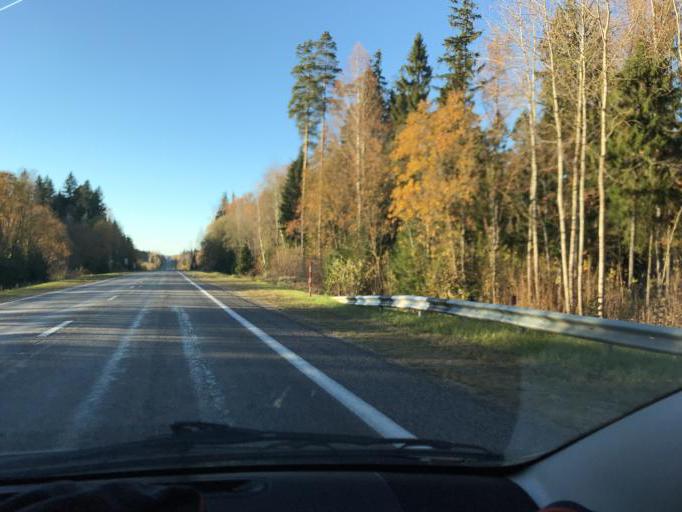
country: BY
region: Vitebsk
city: Vitebsk
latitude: 55.3416
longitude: 30.2313
